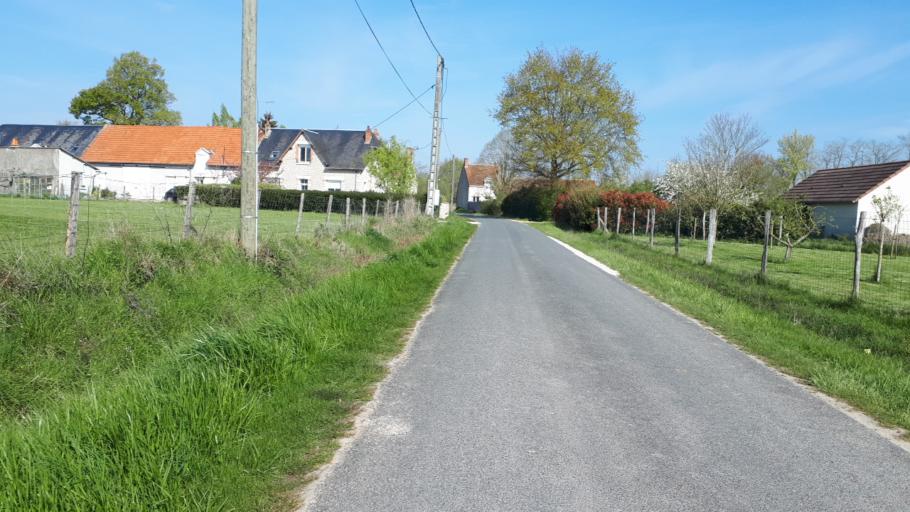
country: FR
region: Centre
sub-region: Departement du Loir-et-Cher
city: Contres
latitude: 47.3810
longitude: 1.3926
